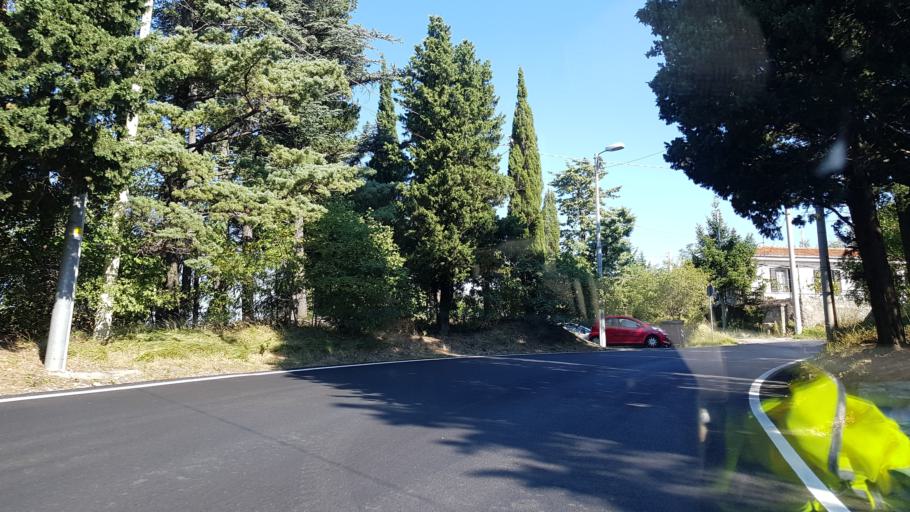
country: IT
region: Friuli Venezia Giulia
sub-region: Provincia di Trieste
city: Villa Opicina
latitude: 45.6667
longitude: 13.7861
